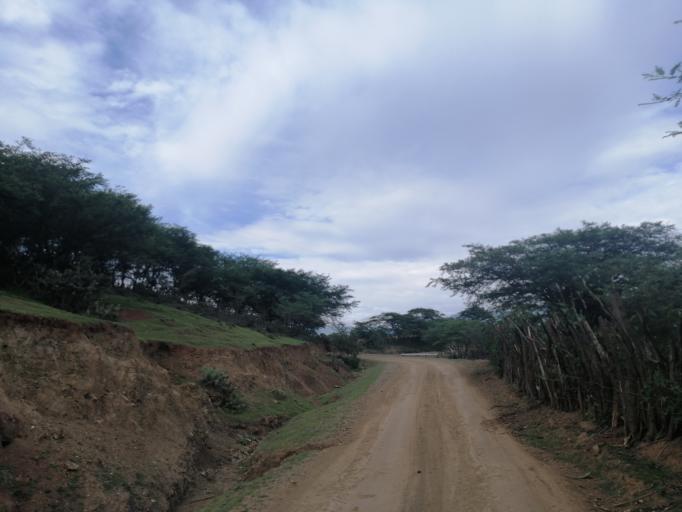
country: EC
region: Loja
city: Catacocha
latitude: -4.0094
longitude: -79.6929
